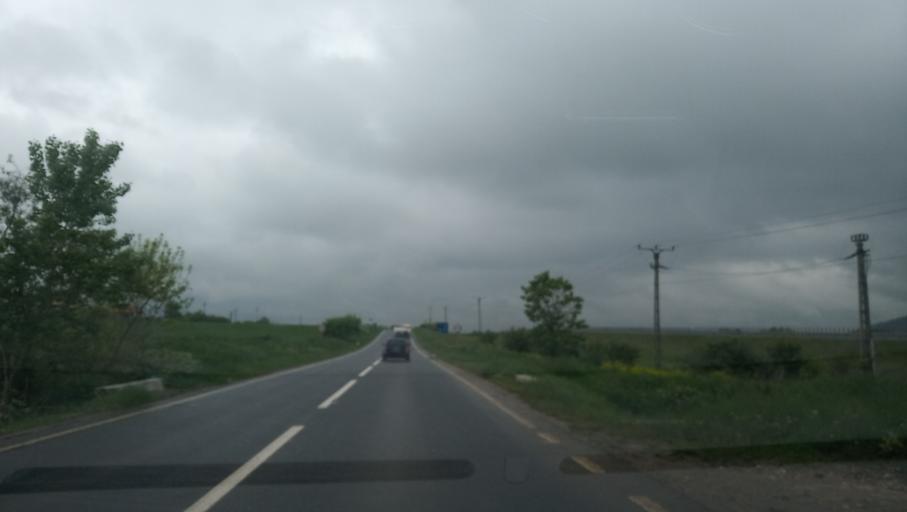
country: RO
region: Alba
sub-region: Comuna Cut
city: Cut
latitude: 45.9216
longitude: 23.6295
